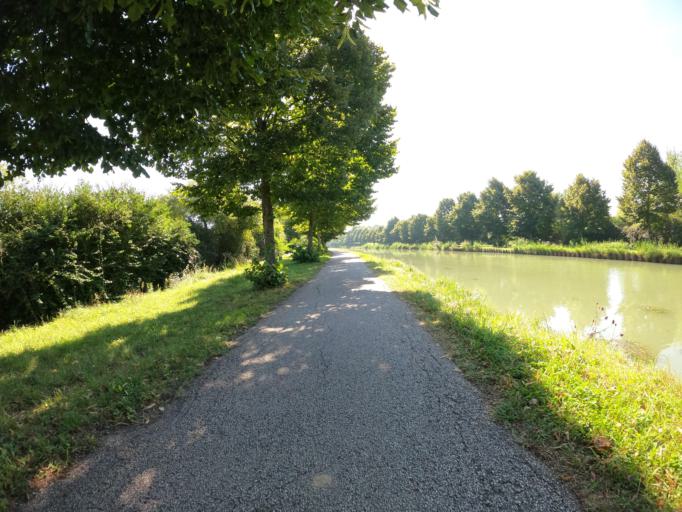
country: FR
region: Aquitaine
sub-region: Departement du Lot-et-Garonne
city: Agen
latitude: 44.1955
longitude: 0.6471
